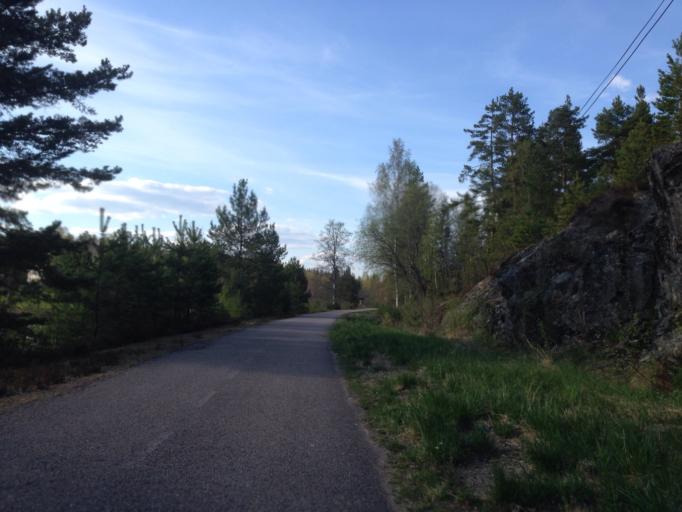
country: SE
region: Dalarna
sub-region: Ludvika Kommun
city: Ludvika
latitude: 60.1651
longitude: 15.1624
